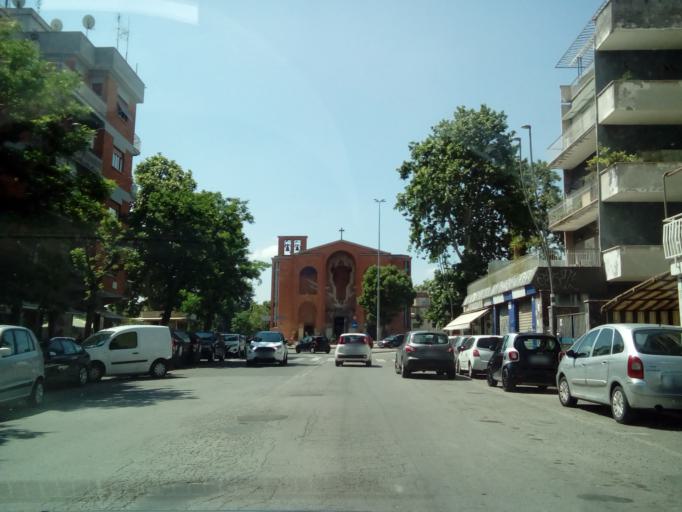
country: IT
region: Latium
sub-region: Citta metropolitana di Roma Capitale
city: Rome
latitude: 41.8779
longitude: 12.5664
